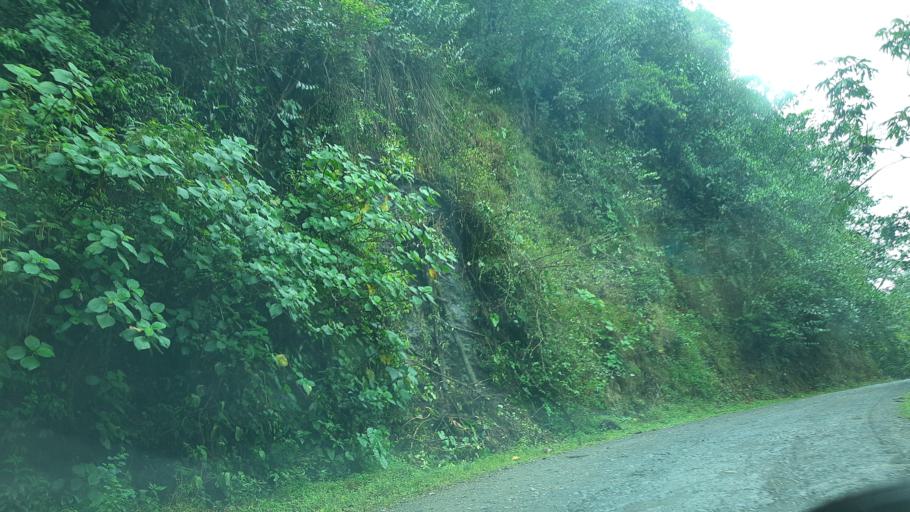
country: CO
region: Boyaca
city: Santa Maria
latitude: 4.9093
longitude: -73.3061
